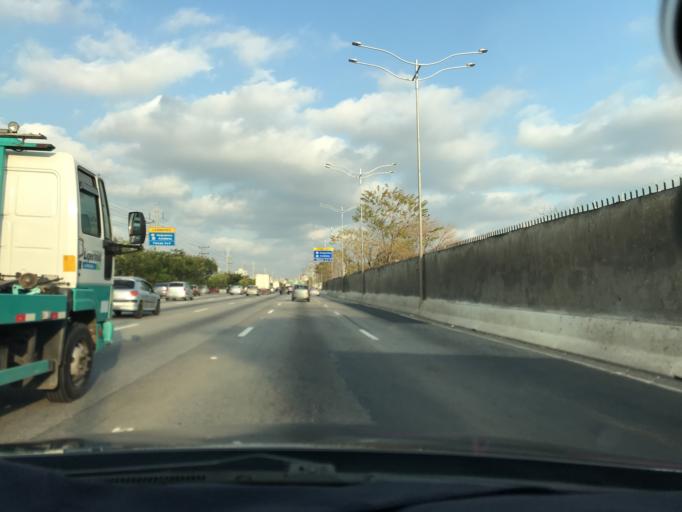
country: BR
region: Sao Paulo
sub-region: Osasco
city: Osasco
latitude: -23.5530
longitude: -46.7246
